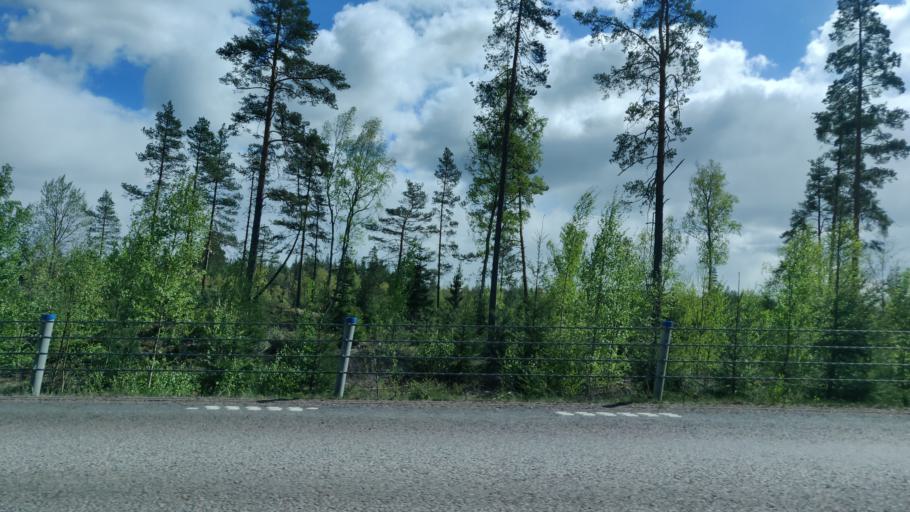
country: SE
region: Vaermland
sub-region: Karlstads Kommun
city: Molkom
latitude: 59.5852
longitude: 13.6834
